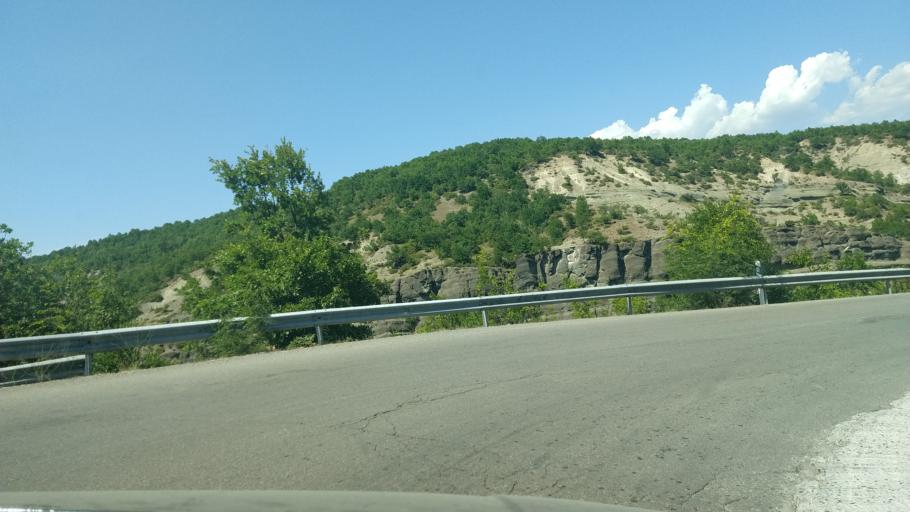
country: GR
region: West Macedonia
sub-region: Nomos Grevenon
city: Grevena
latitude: 40.0503
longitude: 21.4805
